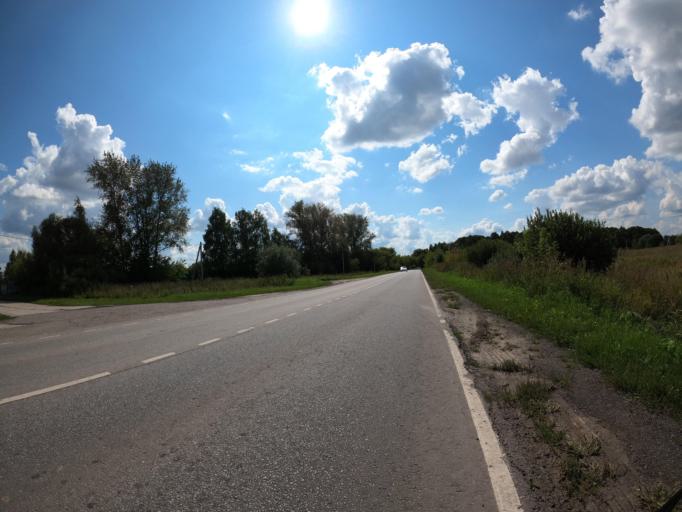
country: RU
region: Moskovskaya
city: Voskresensk
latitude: 55.2759
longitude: 38.6567
